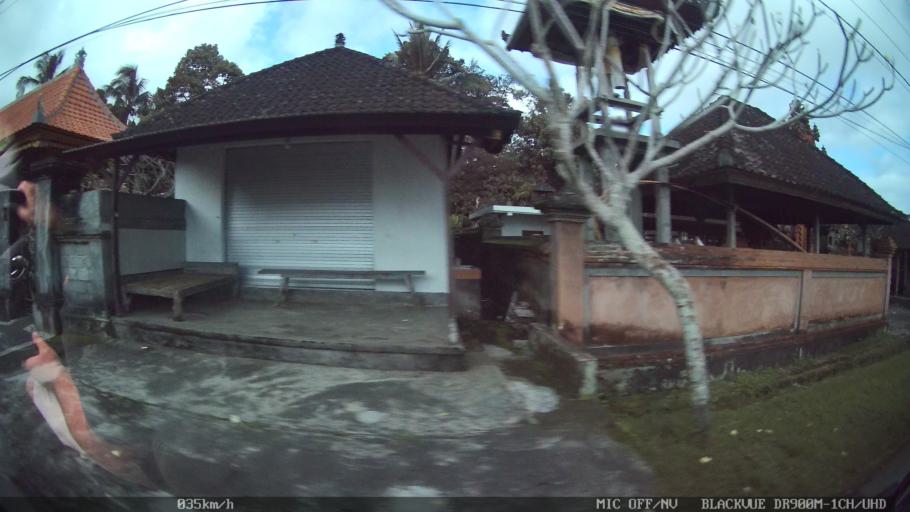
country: ID
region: Bali
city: Banjar Pesalakan
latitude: -8.4937
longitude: 115.3047
